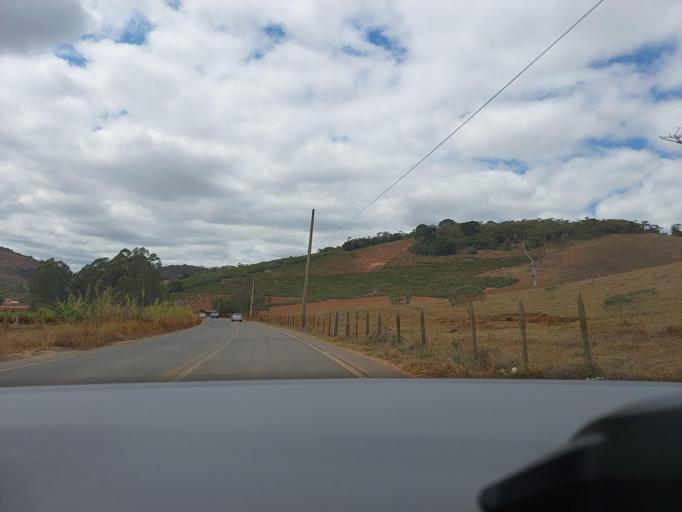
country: BR
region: Minas Gerais
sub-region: Vicosa
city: Vicosa
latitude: -20.8442
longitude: -42.6847
